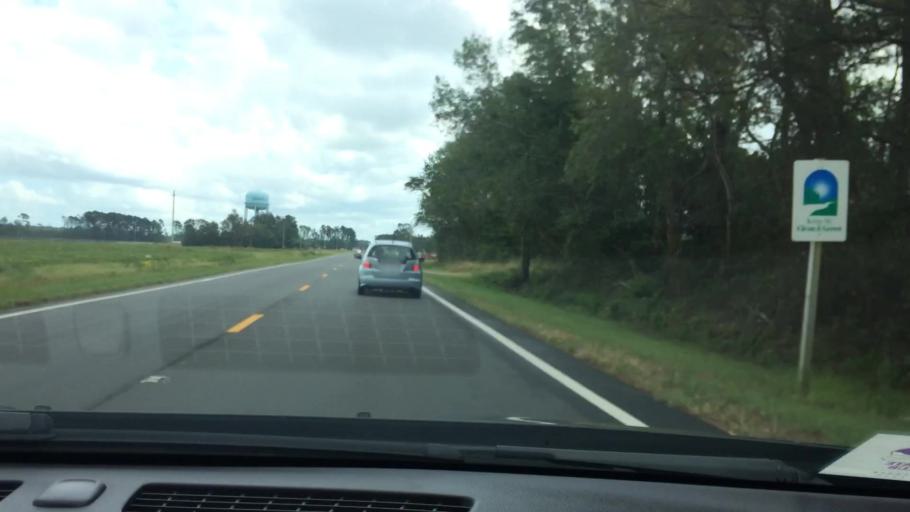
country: US
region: North Carolina
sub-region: Pitt County
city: Farmville
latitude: 35.6010
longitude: -77.6420
